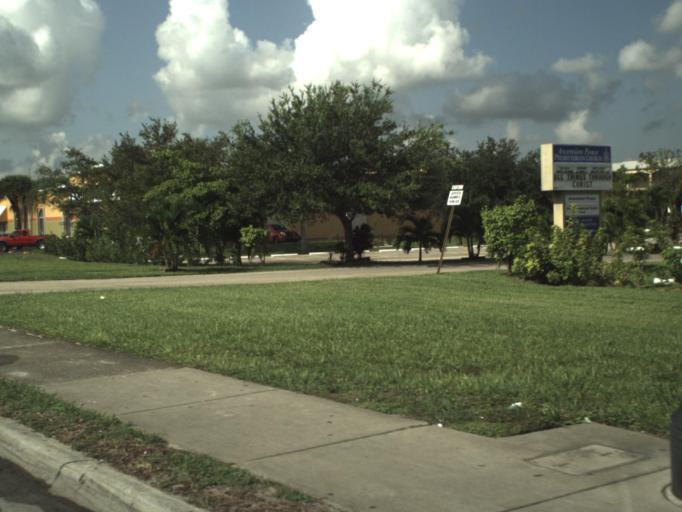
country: US
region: Florida
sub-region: Broward County
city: Lauderdale Lakes
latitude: 26.1612
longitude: -80.2032
